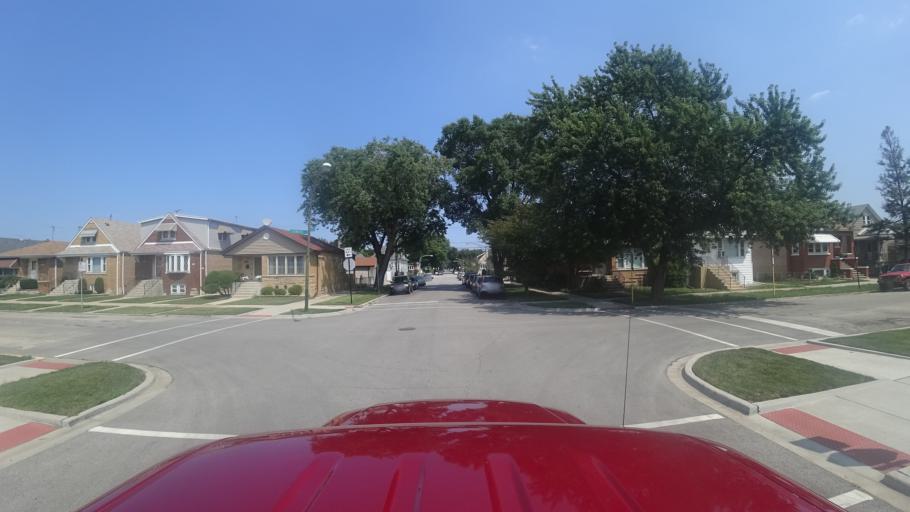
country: US
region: Illinois
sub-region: Cook County
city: Cicero
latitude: 41.7986
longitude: -87.7345
